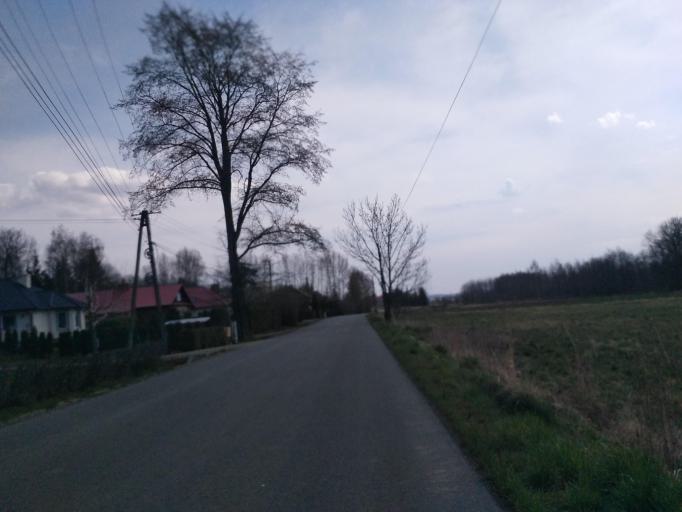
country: PL
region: Subcarpathian Voivodeship
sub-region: Powiat ropczycko-sedziszowski
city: Iwierzyce
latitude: 50.0347
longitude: 21.7541
